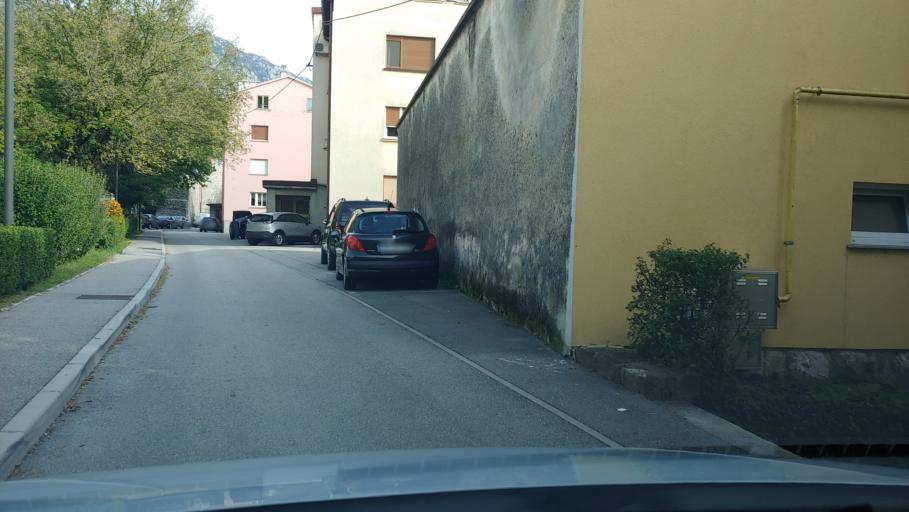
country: SI
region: Ajdovscina
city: Ajdovscina
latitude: 45.8878
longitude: 13.9029
